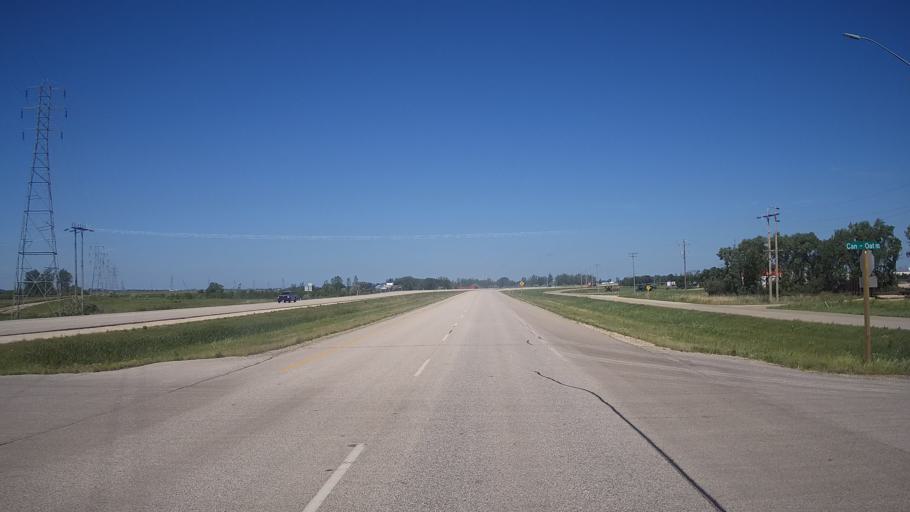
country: CA
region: Manitoba
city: Portage la Prairie
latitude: 49.9604
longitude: -98.3457
